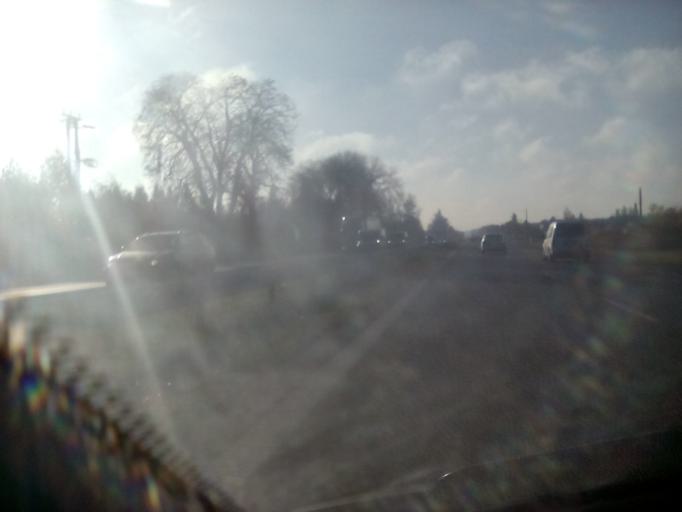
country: PL
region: Masovian Voivodeship
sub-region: Powiat piaseczynski
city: Tarczyn
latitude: 51.9343
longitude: 20.8479
